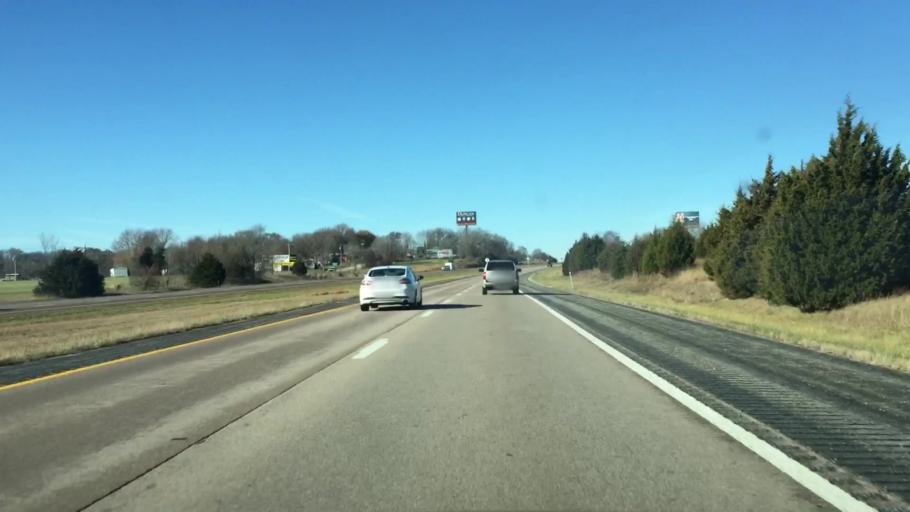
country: US
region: Missouri
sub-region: Miller County
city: Eldon
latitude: 38.3682
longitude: -92.5145
